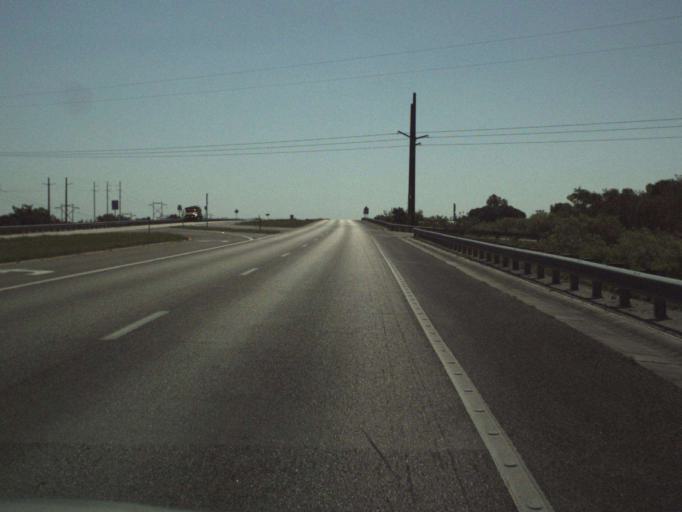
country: US
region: Florida
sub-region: Brevard County
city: Cocoa West
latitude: 28.3696
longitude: -80.8772
